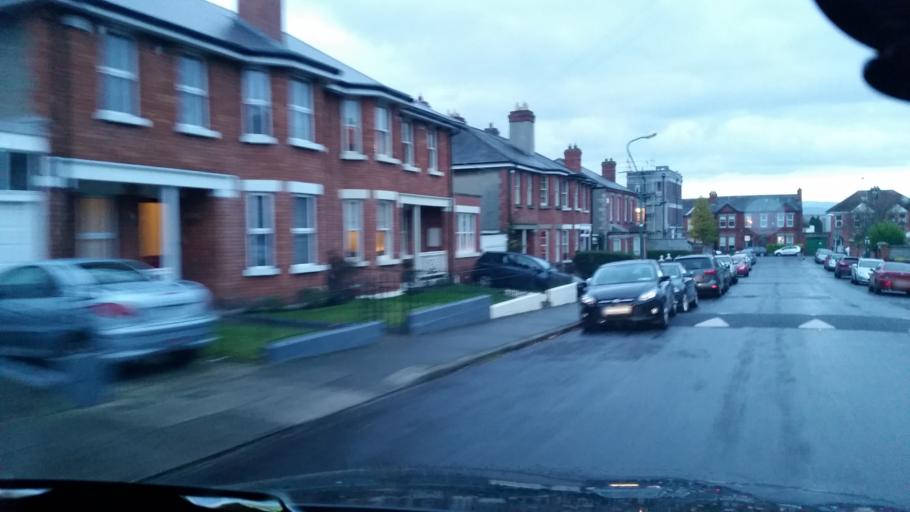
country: IE
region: Leinster
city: Drumcondra
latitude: 53.3752
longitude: -6.2552
